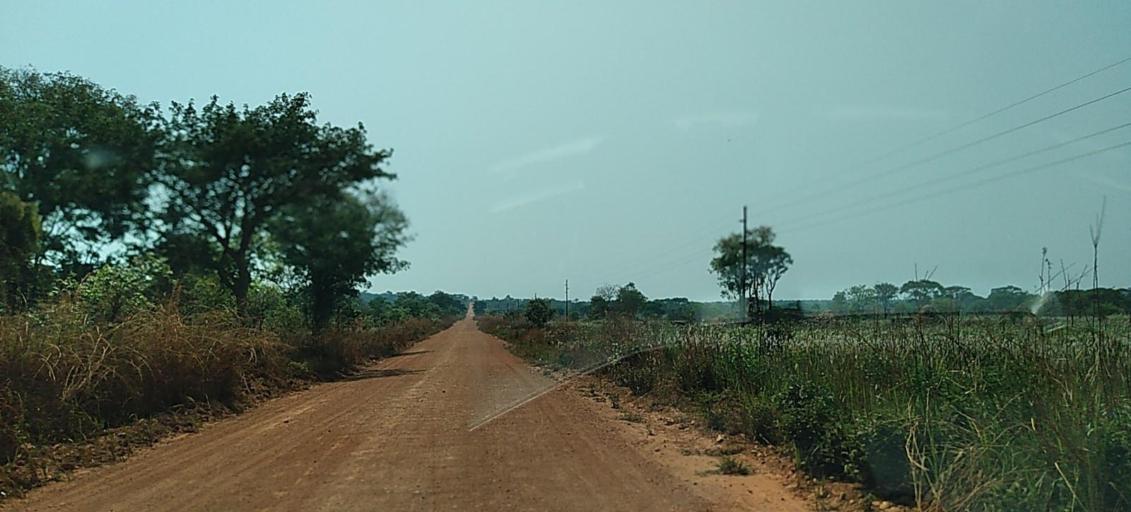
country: ZM
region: North-Western
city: Kansanshi
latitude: -12.0045
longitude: 26.5623
